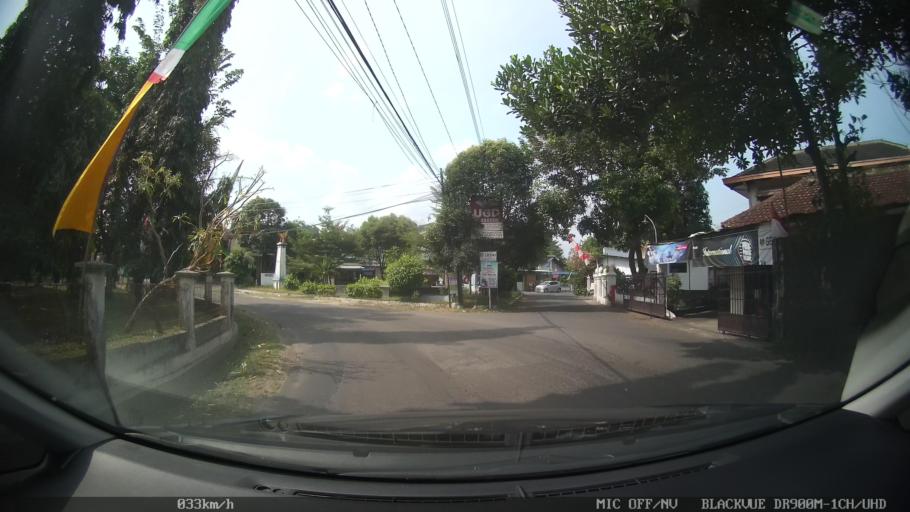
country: ID
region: Daerah Istimewa Yogyakarta
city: Depok
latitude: -7.7884
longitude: 110.4480
